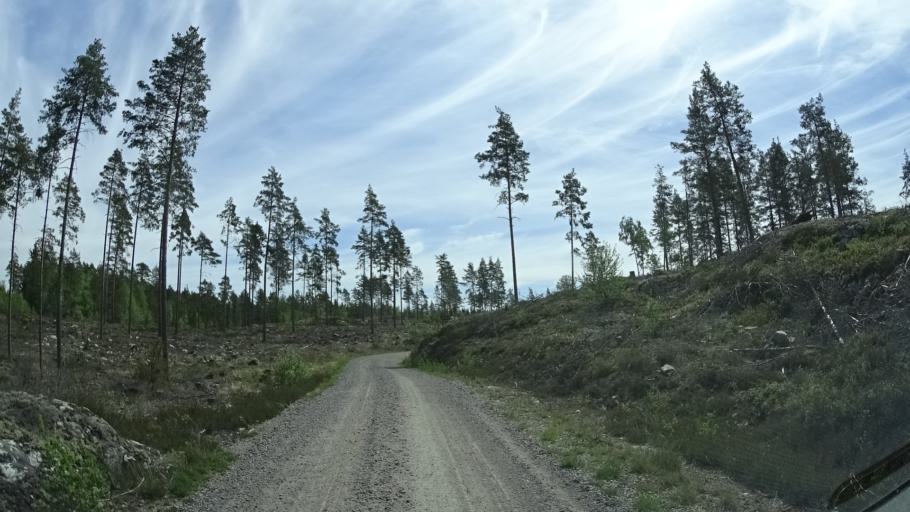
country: SE
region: OEstergoetland
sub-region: Finspangs Kommun
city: Finspang
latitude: 58.7733
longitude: 15.8454
